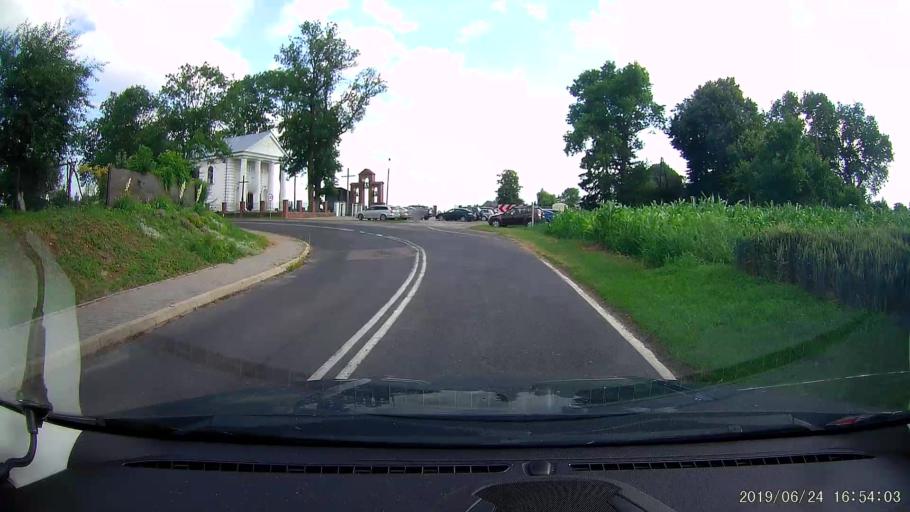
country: PL
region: Lublin Voivodeship
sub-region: Powiat tomaszowski
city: Telatyn
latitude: 50.5331
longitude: 23.8086
